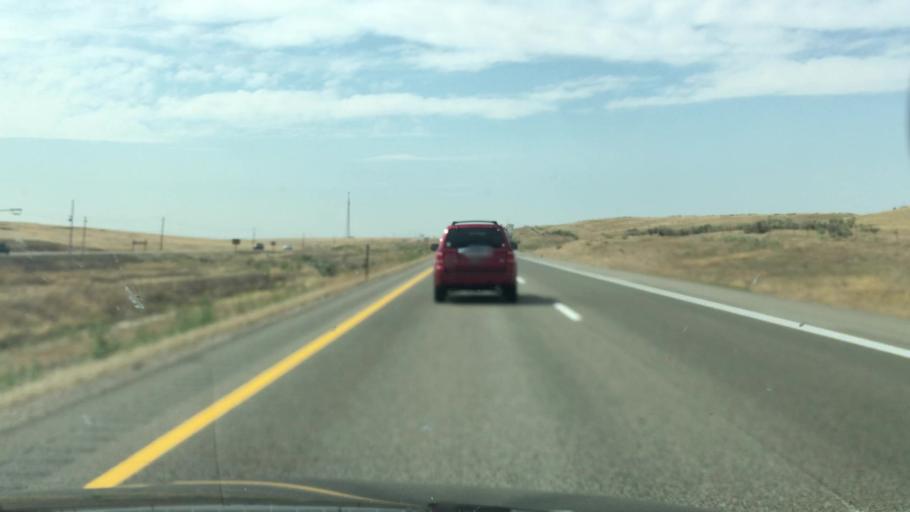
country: US
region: Idaho
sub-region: Ada County
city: Boise
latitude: 43.4414
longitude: -116.0682
